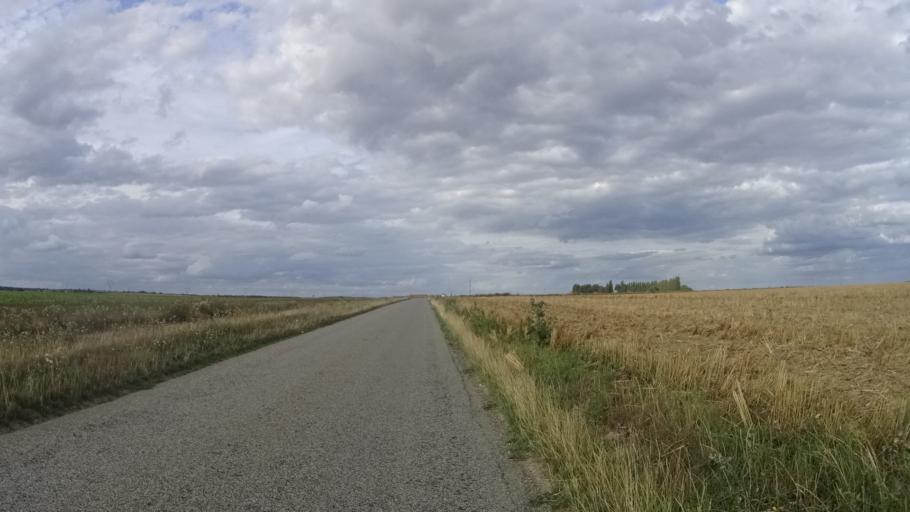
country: FR
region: Picardie
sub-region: Departement de l'Oise
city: Lagny-le-Sec
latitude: 49.1043
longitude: 2.7188
